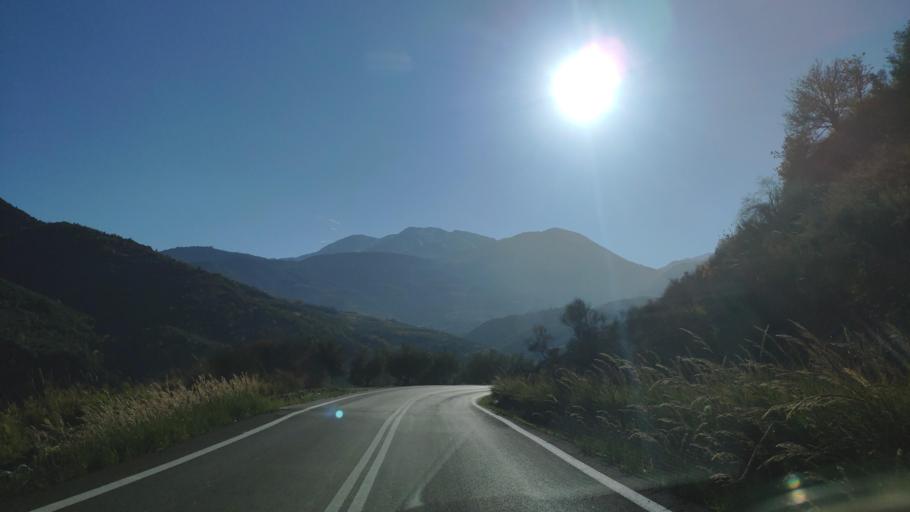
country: GR
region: Peloponnese
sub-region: Nomos Korinthias
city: Xylokastro
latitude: 38.0046
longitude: 22.5064
